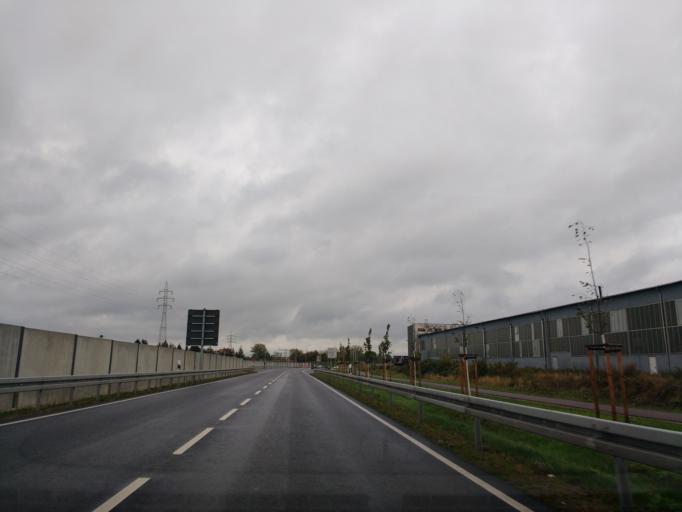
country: DE
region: Saxony-Anhalt
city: Halle (Saale)
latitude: 51.4823
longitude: 12.0182
